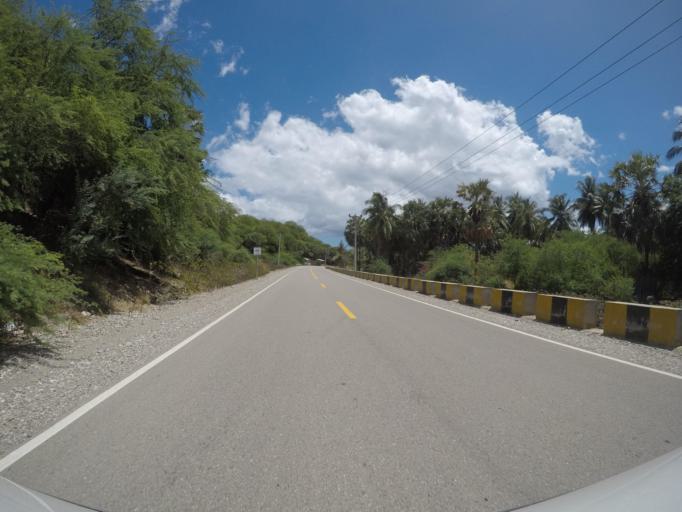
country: TL
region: Lautem
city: Lospalos
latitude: -8.4136
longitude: 126.7425
